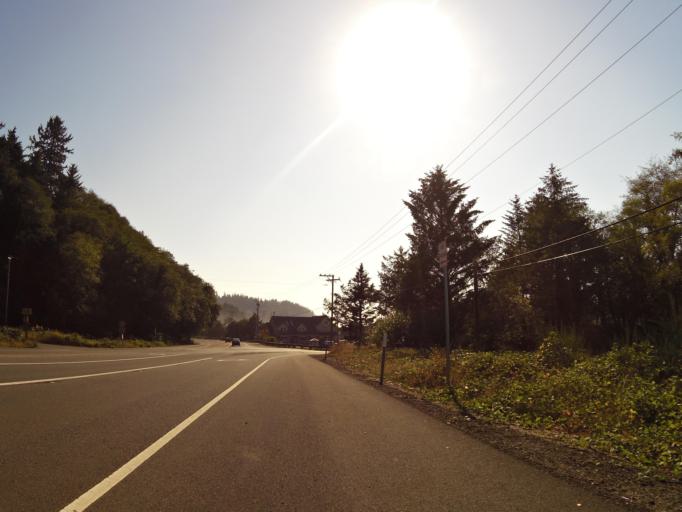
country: US
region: Oregon
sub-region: Tillamook County
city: Pacific City
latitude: 45.1038
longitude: -123.9805
